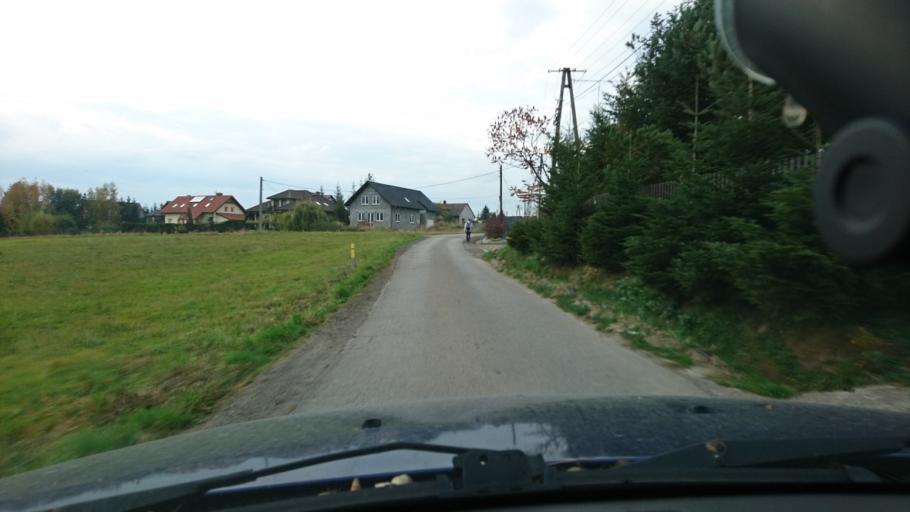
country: PL
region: Silesian Voivodeship
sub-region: Powiat bielski
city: Kozy
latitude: 49.8640
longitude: 19.1587
